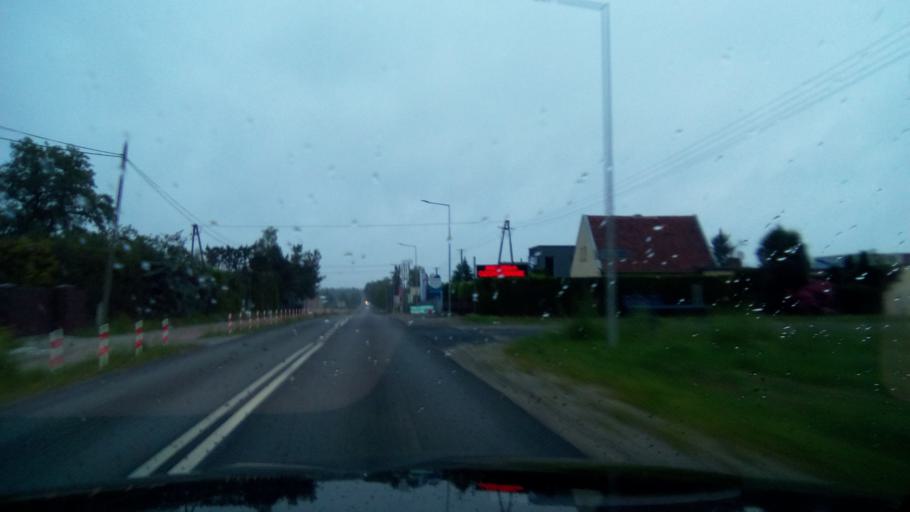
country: PL
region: Greater Poland Voivodeship
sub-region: Powiat poznanski
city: Kobylnica
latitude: 52.4353
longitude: 17.0736
